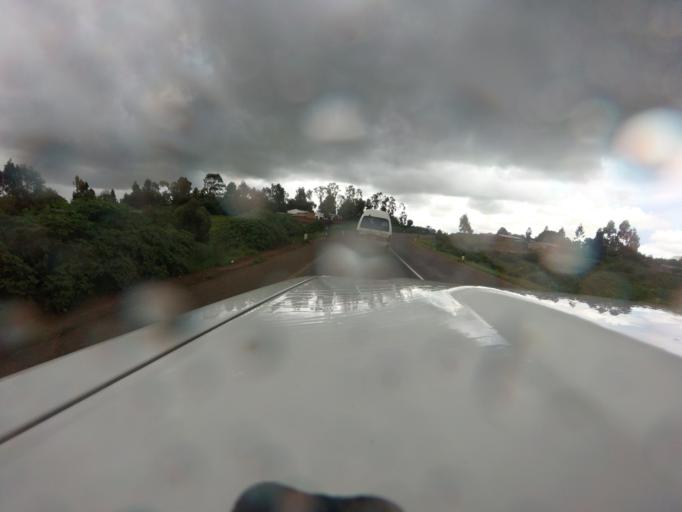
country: MW
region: Central Region
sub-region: Dedza District
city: Dedza
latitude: -14.3952
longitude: 34.3894
